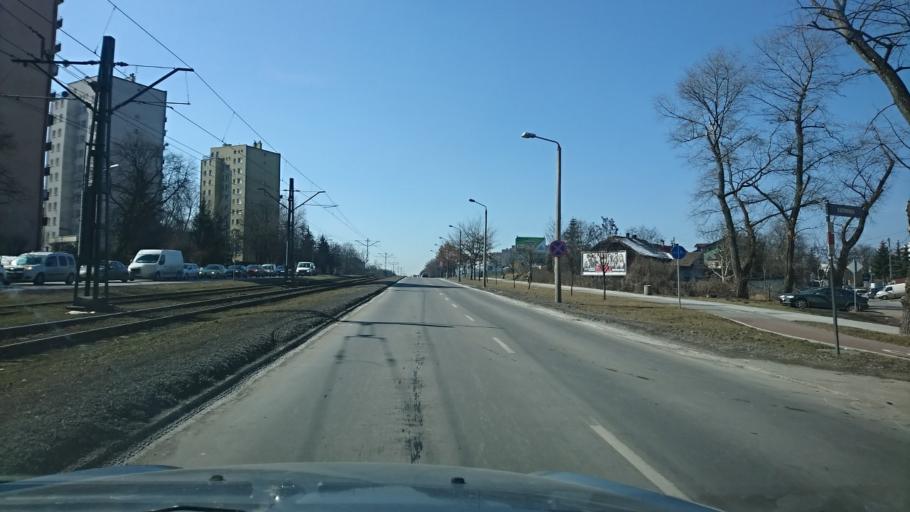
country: PL
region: Lesser Poland Voivodeship
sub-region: Powiat wielicki
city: Kokotow
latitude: 50.0847
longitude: 20.0376
